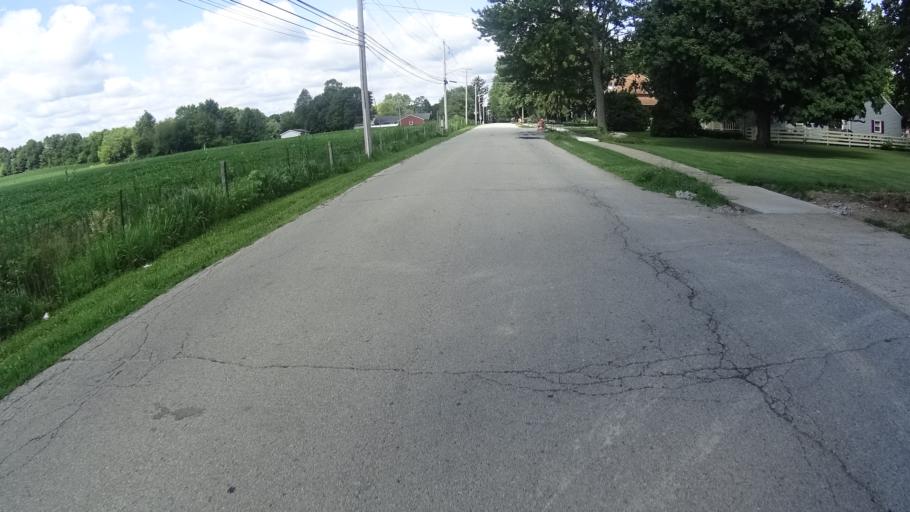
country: US
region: Indiana
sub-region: Madison County
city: Pendleton
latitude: 39.9964
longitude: -85.7389
